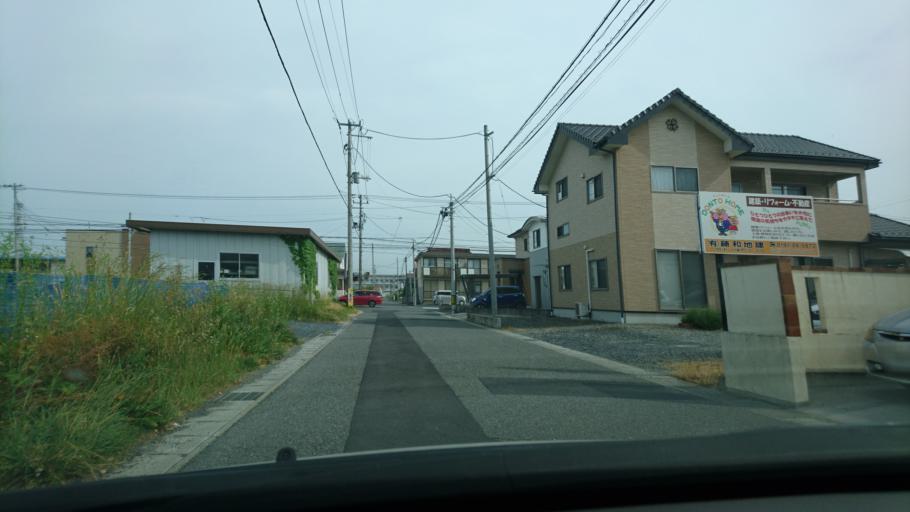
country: JP
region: Iwate
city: Ichinoseki
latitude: 38.9208
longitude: 141.1073
